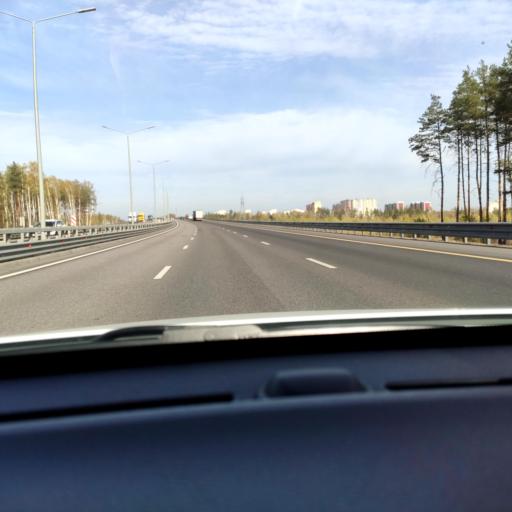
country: RU
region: Voronezj
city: Somovo
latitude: 51.7295
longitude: 39.3114
